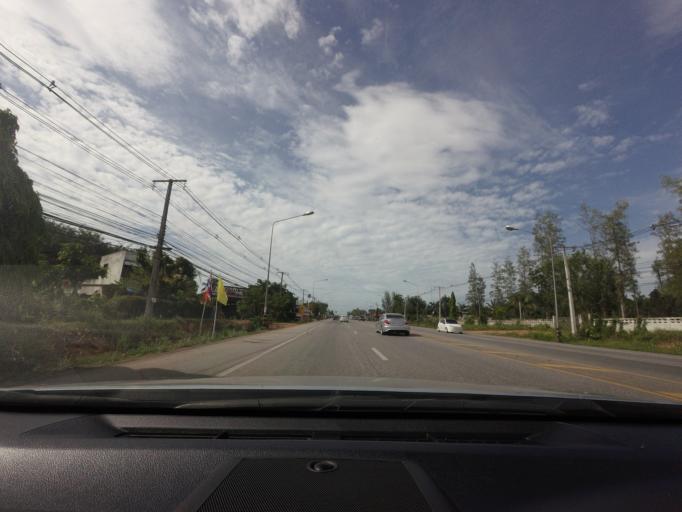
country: TH
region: Songkhla
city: Khlong Hoi Khong
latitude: 6.9560
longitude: 100.4209
